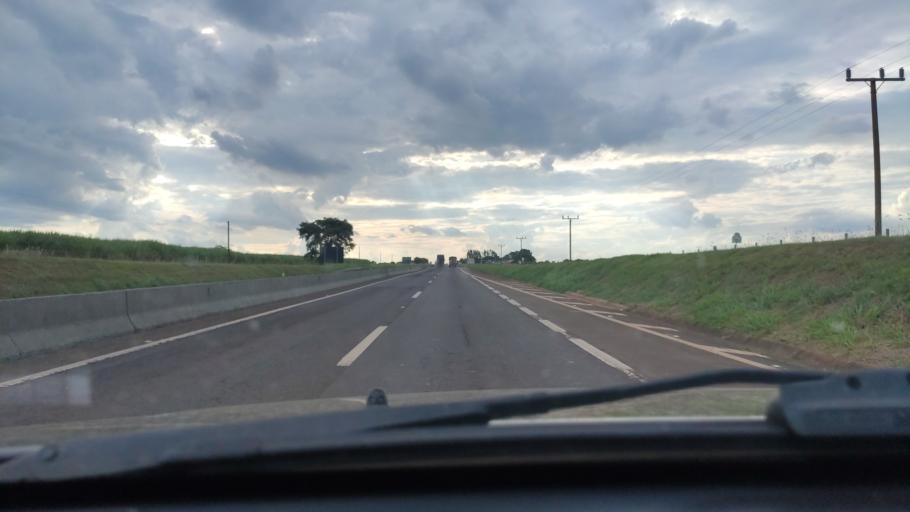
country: BR
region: Sao Paulo
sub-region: Palmital
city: Palmital
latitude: -22.7016
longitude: -50.2800
